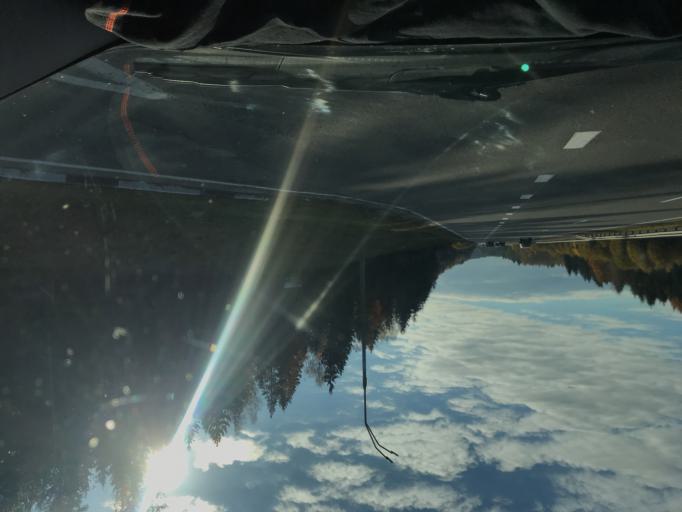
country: BY
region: Minsk
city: Lahoysk
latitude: 54.1325
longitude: 27.8082
